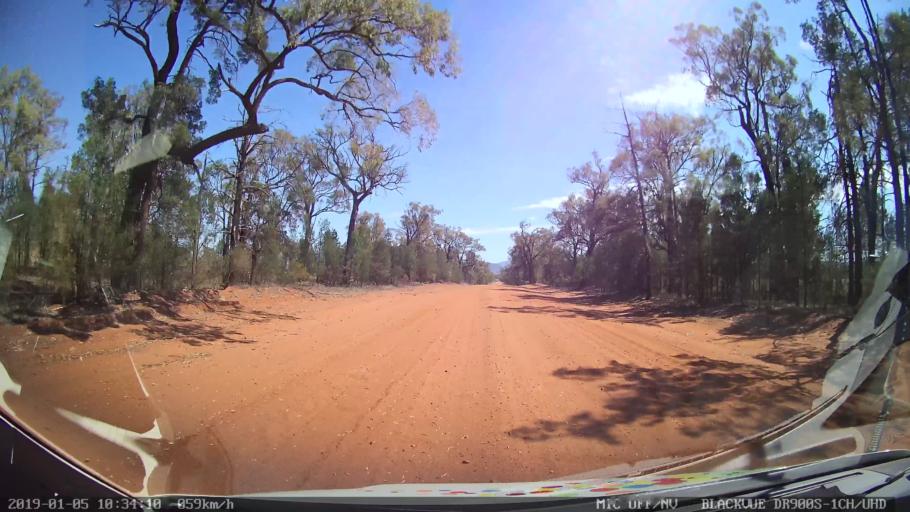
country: AU
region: New South Wales
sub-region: Gilgandra
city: Gilgandra
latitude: -31.5004
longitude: 148.9290
